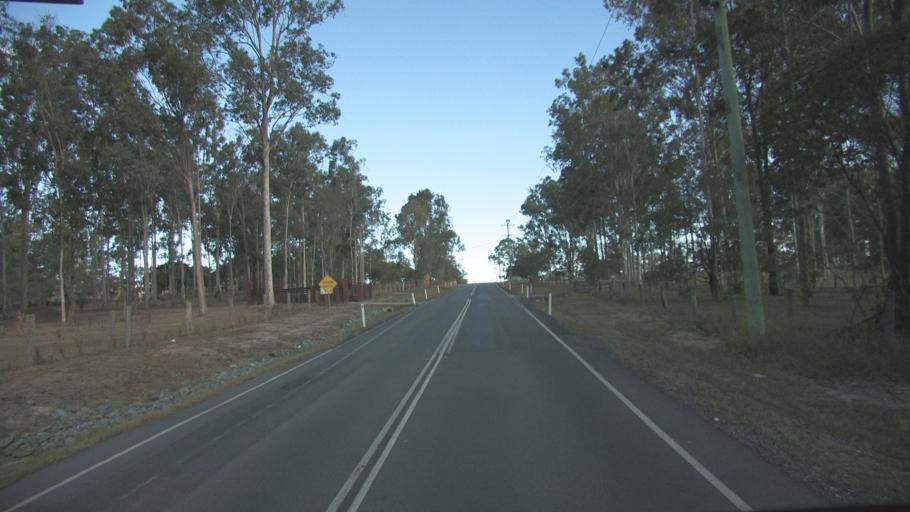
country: AU
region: Queensland
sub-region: Logan
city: Cedar Vale
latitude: -27.8293
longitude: 153.0532
